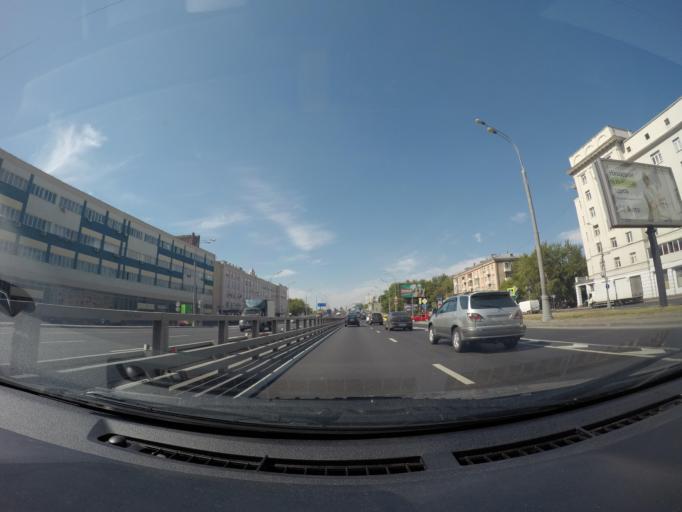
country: RU
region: Moscow
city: Ryazanskiy
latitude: 55.7262
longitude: 37.7604
